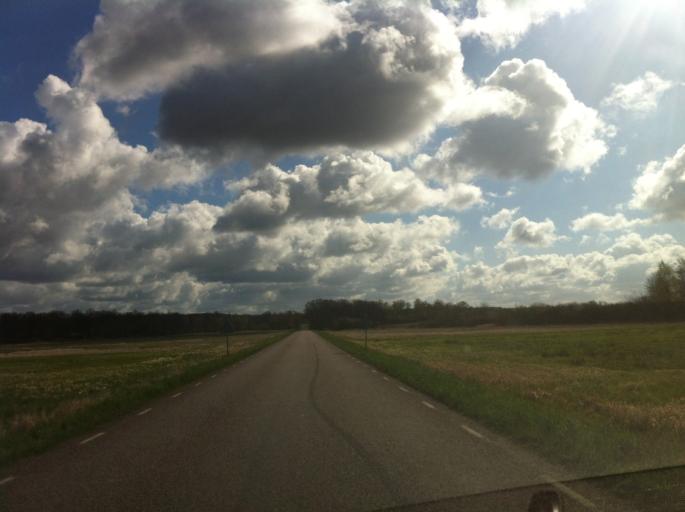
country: SE
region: Skane
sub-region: Eslovs Kommun
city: Stehag
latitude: 55.9124
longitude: 13.4417
